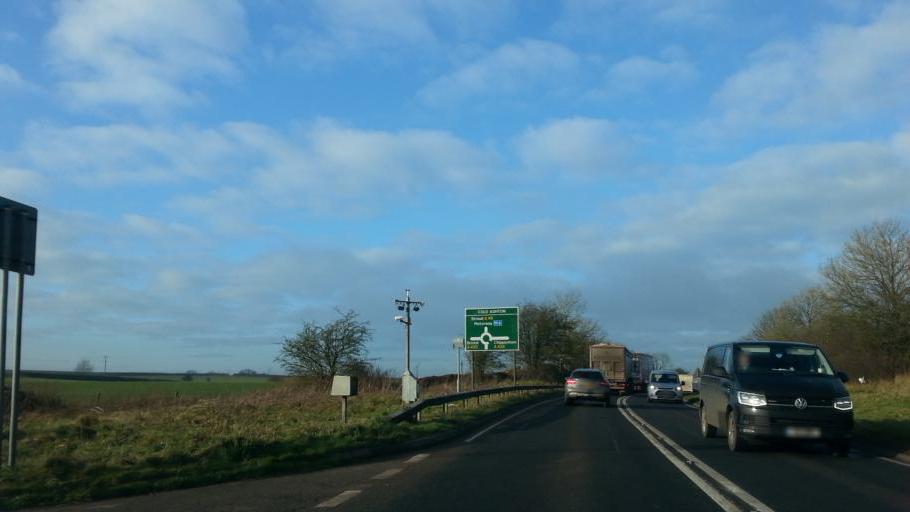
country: GB
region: England
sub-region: South Gloucestershire
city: Cold Ashton
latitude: 51.4510
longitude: -2.3678
